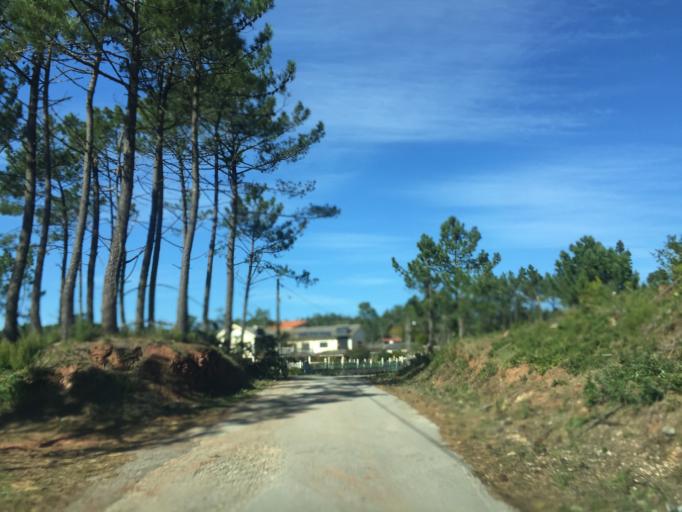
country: PT
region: Coimbra
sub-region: Figueira da Foz
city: Tavarede
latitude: 40.1855
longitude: -8.8388
